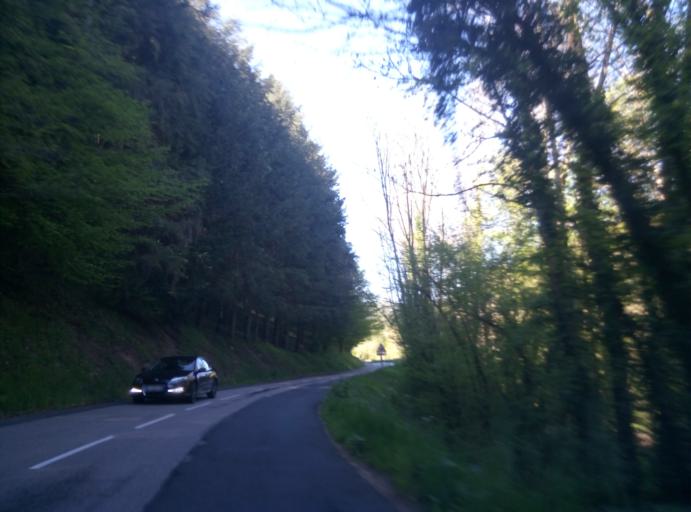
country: FR
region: Rhone-Alpes
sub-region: Departement du Rhone
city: Grandris
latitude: 46.0017
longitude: 4.4960
